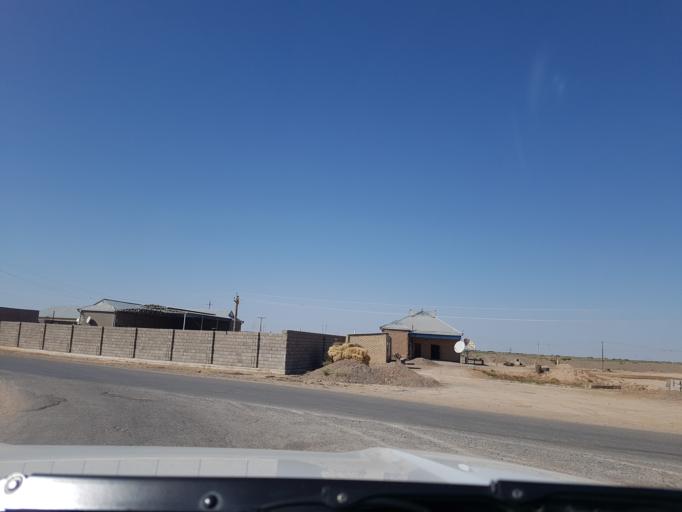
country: IR
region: Razavi Khorasan
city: Sarakhs
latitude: 36.5201
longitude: 61.2506
